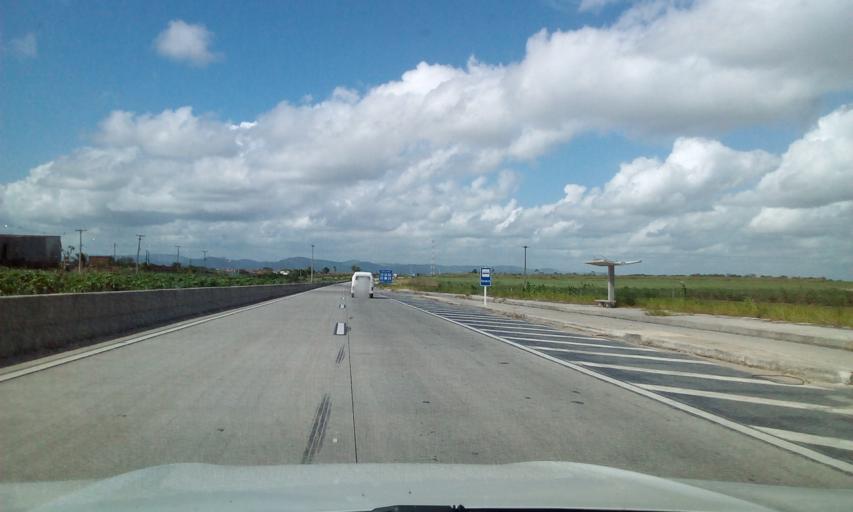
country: BR
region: Alagoas
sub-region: Messias
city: Messias
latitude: -9.3975
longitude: -35.8365
